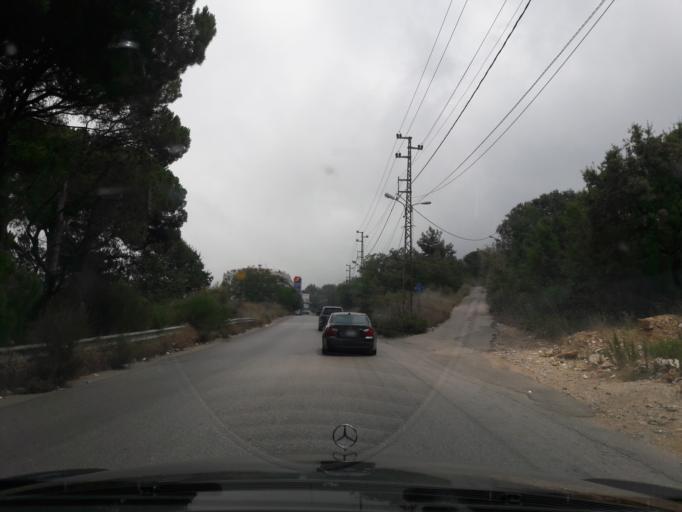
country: LB
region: Mont-Liban
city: Djounie
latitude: 33.9141
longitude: 35.6876
